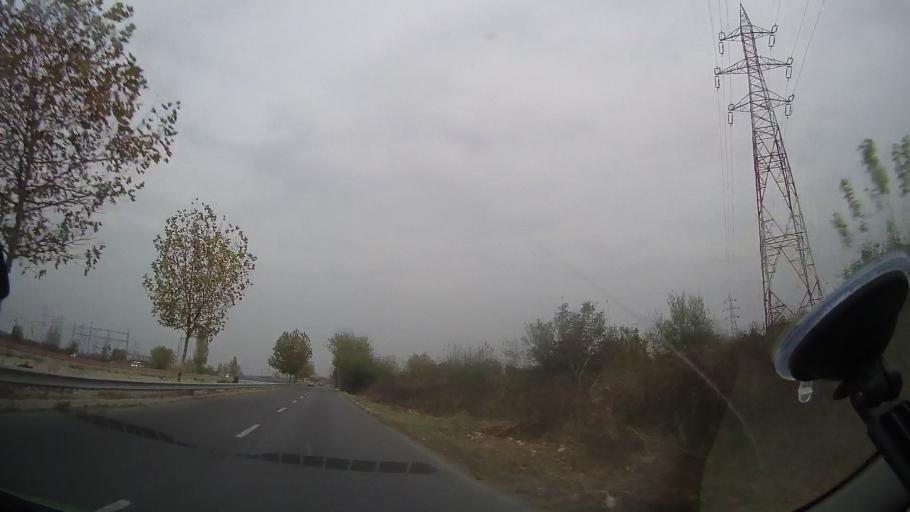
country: RO
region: Ilfov
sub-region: Comuna Popesti-Leordeni
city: Popesti-Leordeni
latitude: 44.3949
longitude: 26.1756
